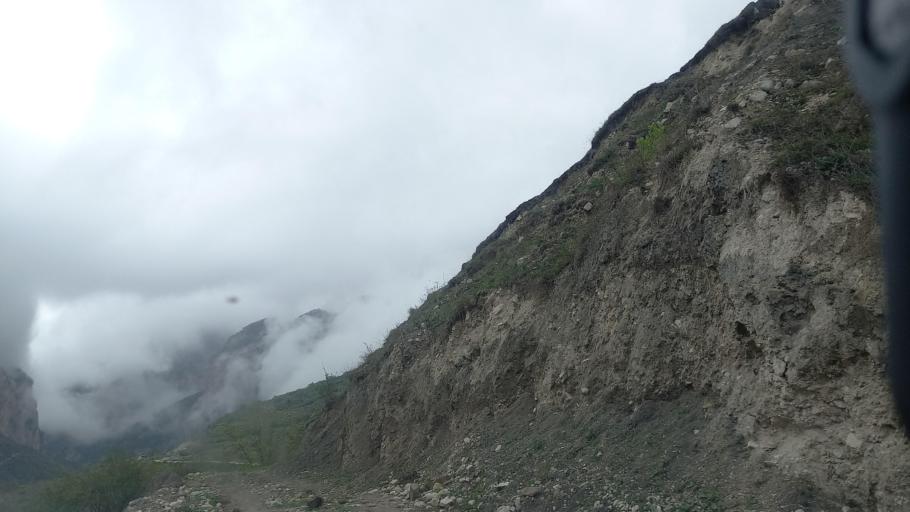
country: RU
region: Kabardino-Balkariya
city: Verkhnyaya Balkariya
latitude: 43.1668
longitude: 43.4944
